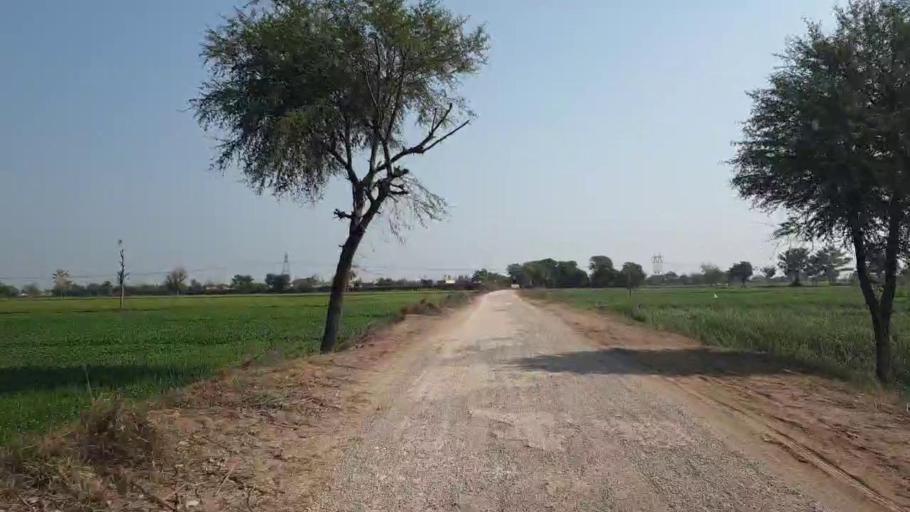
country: PK
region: Sindh
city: Hala
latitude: 25.9104
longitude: 68.4490
